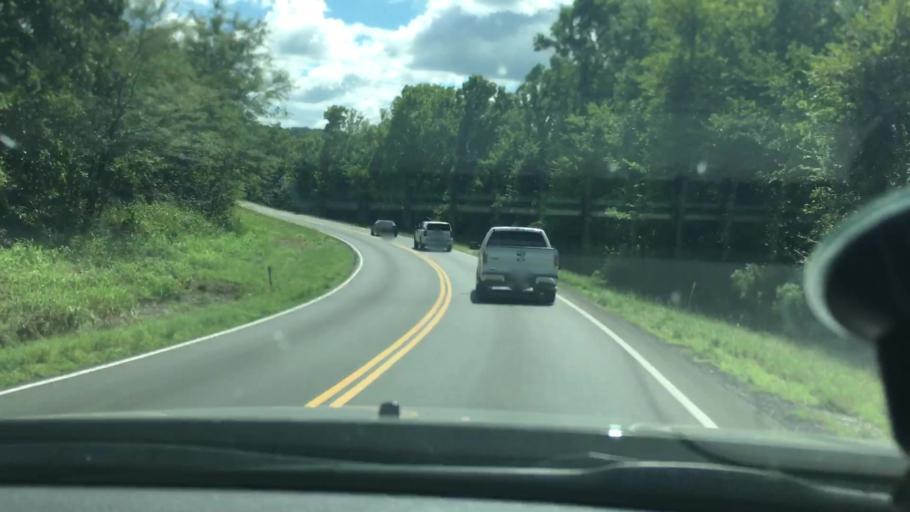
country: US
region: Oklahoma
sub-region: Sequoyah County
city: Vian
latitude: 35.6468
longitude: -94.9599
